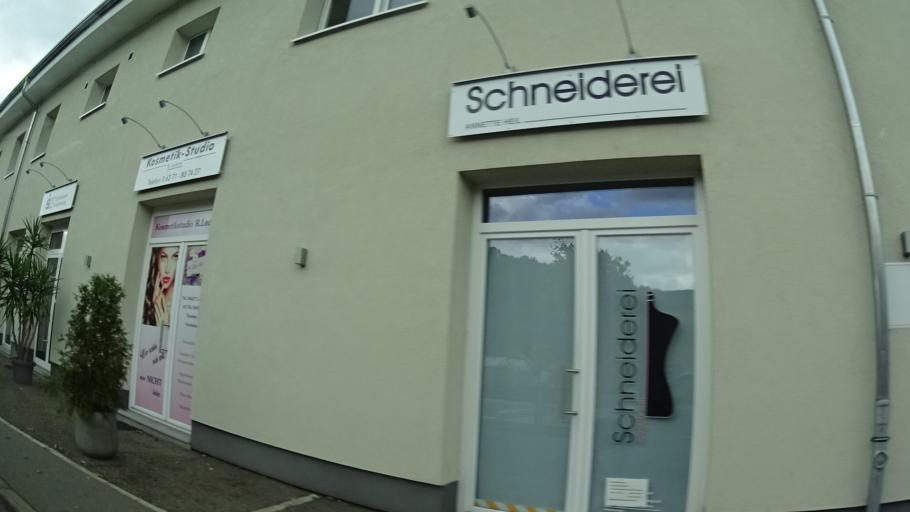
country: DE
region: Baden-Wuerttemberg
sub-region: Karlsruhe Region
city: Eberbach
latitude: 49.4740
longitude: 8.9866
